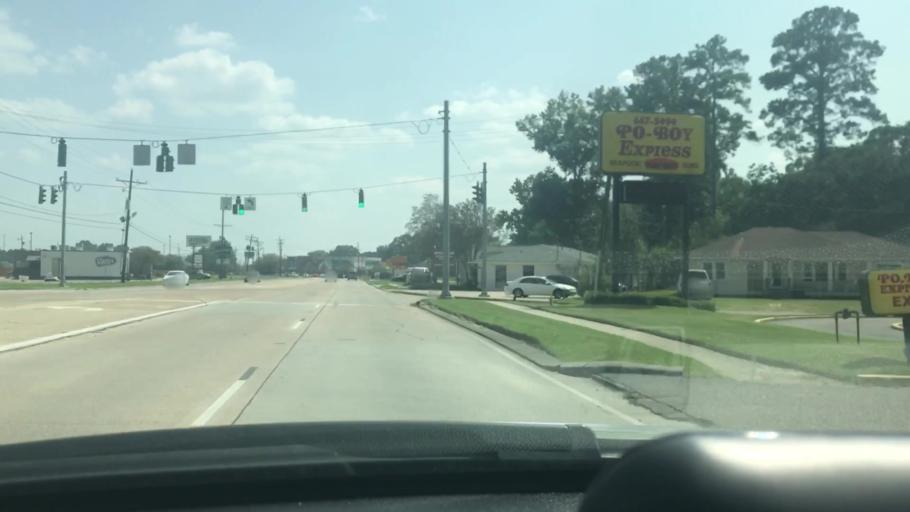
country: US
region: Louisiana
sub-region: Livingston Parish
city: Denham Springs
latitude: 30.4768
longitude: -90.9563
